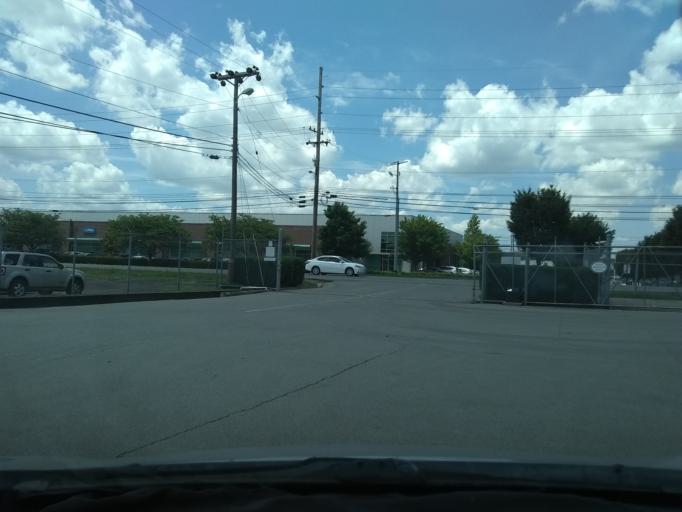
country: US
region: Tennessee
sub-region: Davidson County
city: Nashville
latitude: 36.1447
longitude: -86.7081
